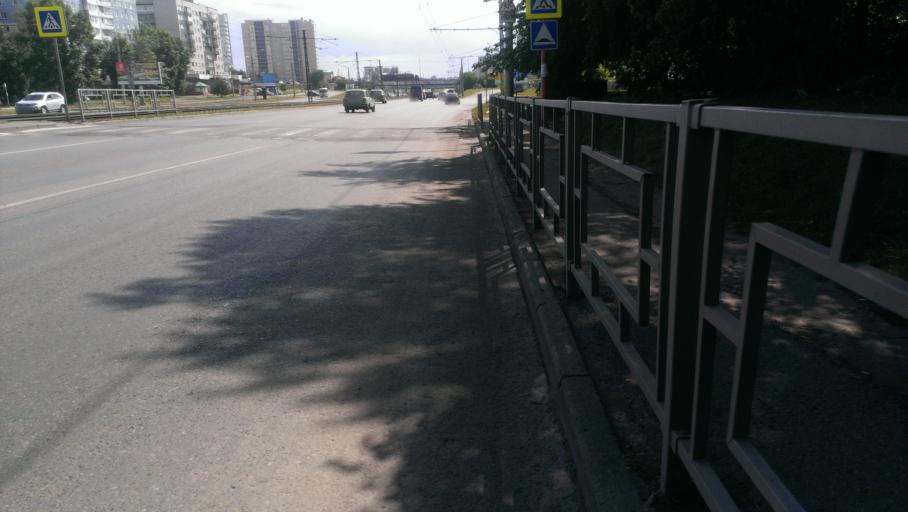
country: RU
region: Altai Krai
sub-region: Gorod Barnaulskiy
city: Barnaul
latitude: 53.3461
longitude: 83.6961
